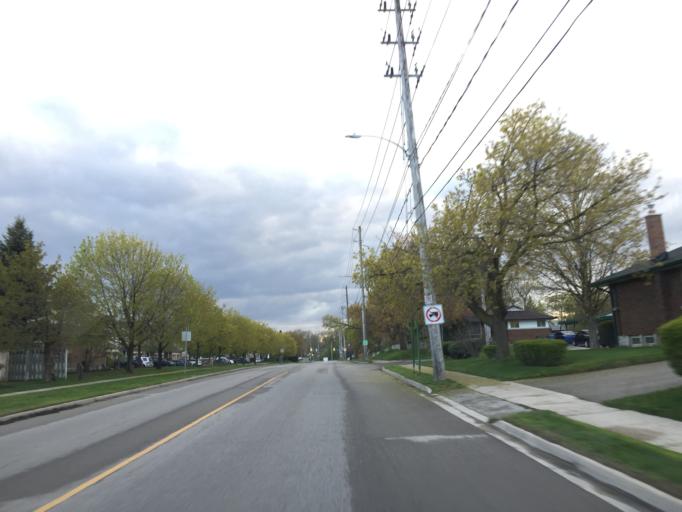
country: CA
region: Ontario
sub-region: Wellington County
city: Guelph
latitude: 43.5452
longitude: -80.2636
